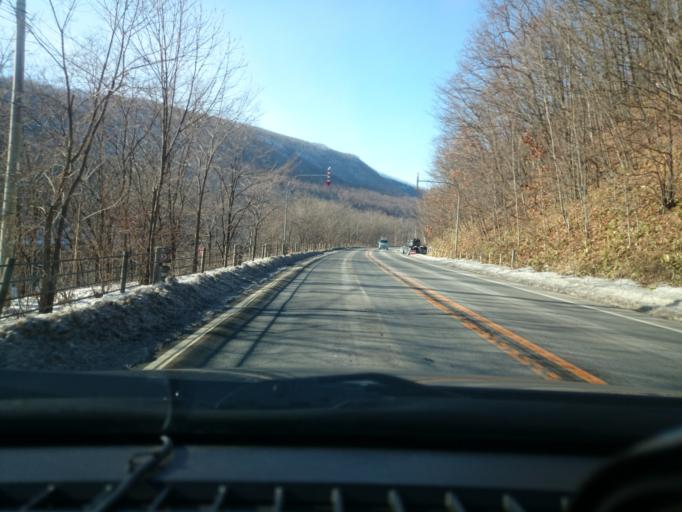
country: JP
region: Hokkaido
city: Otofuke
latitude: 43.2530
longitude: 143.4655
